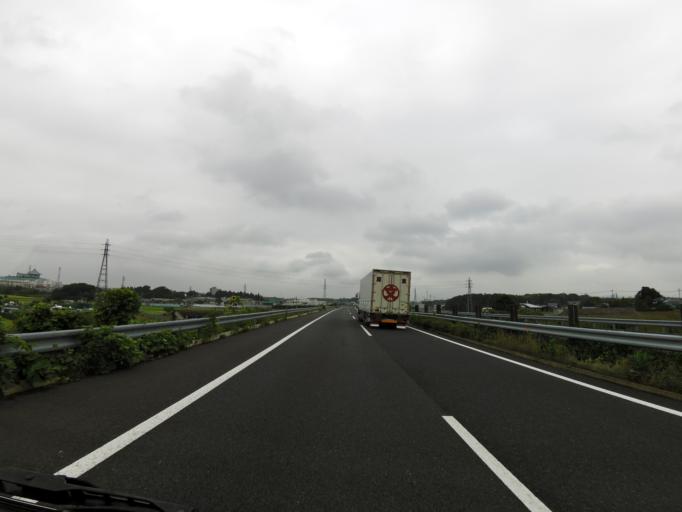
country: JP
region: Tochigi
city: Mooka
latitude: 36.4309
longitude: 139.9734
